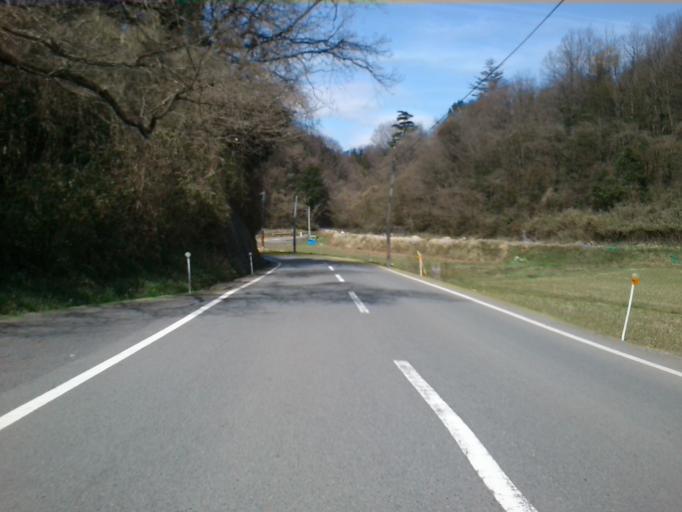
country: JP
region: Nara
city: Nara-shi
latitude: 34.7161
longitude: 135.8887
